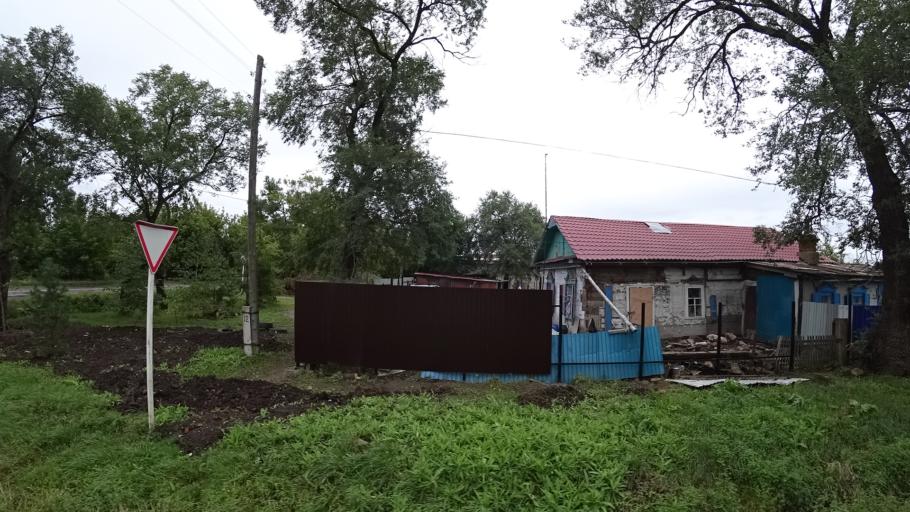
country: RU
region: Primorskiy
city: Chernigovka
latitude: 44.3413
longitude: 132.5691
